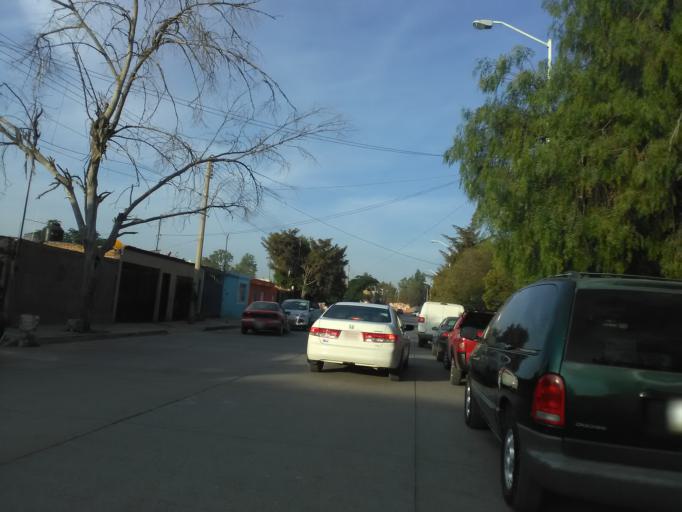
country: MX
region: Durango
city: Victoria de Durango
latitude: 24.0481
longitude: -104.6455
